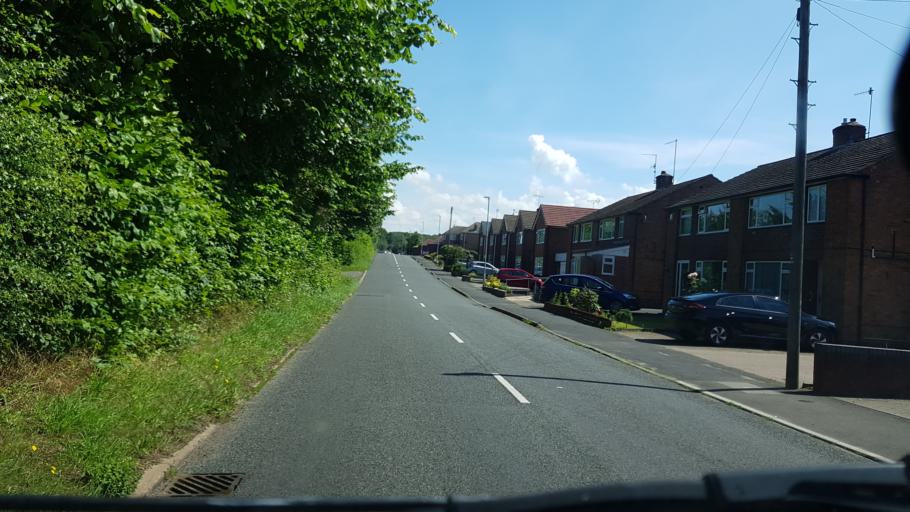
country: GB
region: England
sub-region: Worcestershire
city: Stourport-on-Severn
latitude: 52.3521
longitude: -2.2961
